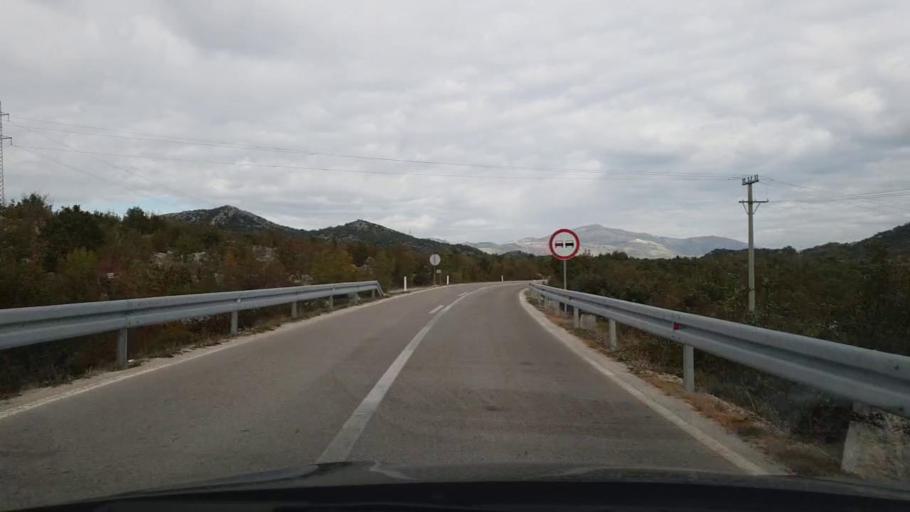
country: HR
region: Dubrovacko-Neretvanska
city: Cibaca
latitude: 42.6639
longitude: 18.2120
